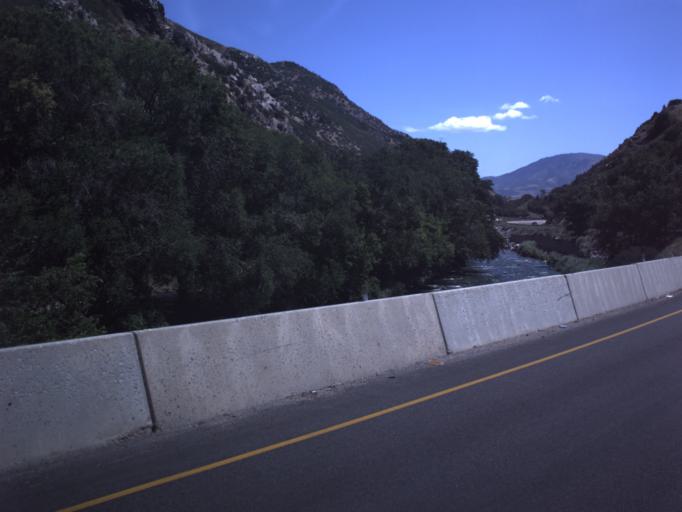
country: US
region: Utah
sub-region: Weber County
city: Uintah
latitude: 41.1372
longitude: -111.8850
